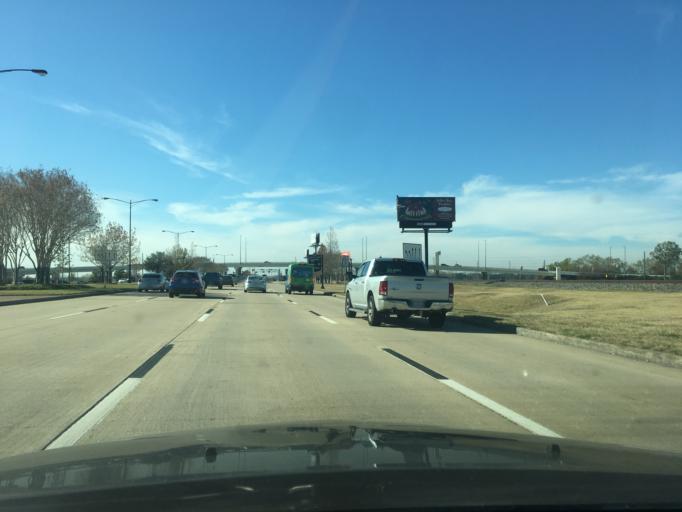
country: US
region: Texas
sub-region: Fort Bend County
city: Sugar Land
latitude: 29.6151
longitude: -95.6463
